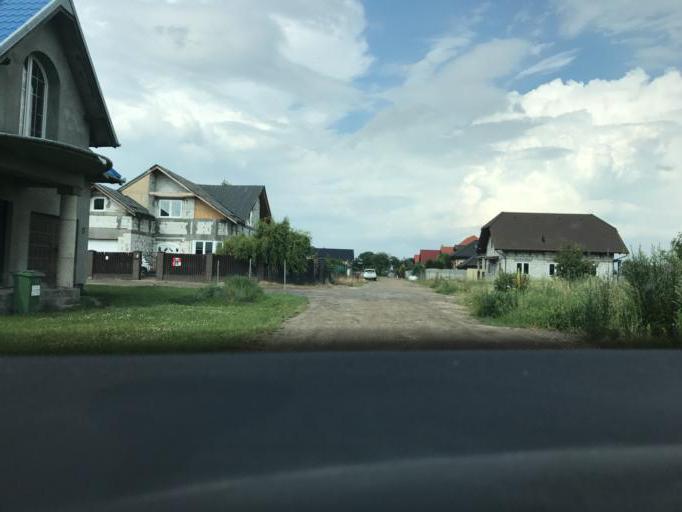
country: PL
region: Pomeranian Voivodeship
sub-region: Powiat gdanski
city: Cedry Wielkie
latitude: 54.3346
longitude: 18.8009
